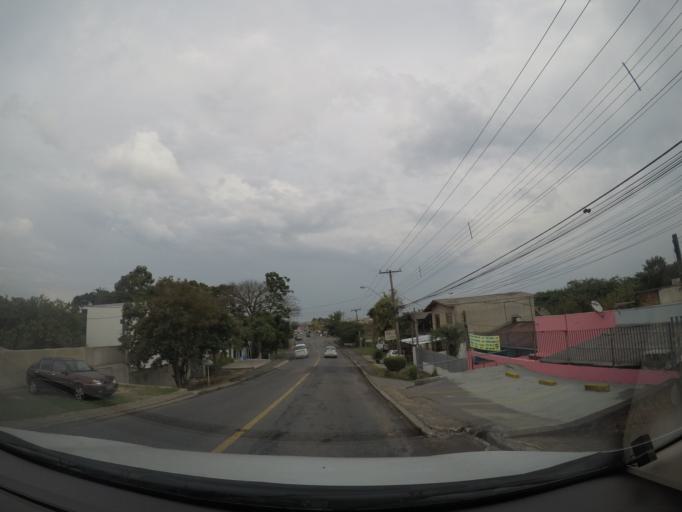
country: BR
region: Parana
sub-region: Sao Jose Dos Pinhais
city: Sao Jose dos Pinhais
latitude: -25.5275
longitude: -49.2604
